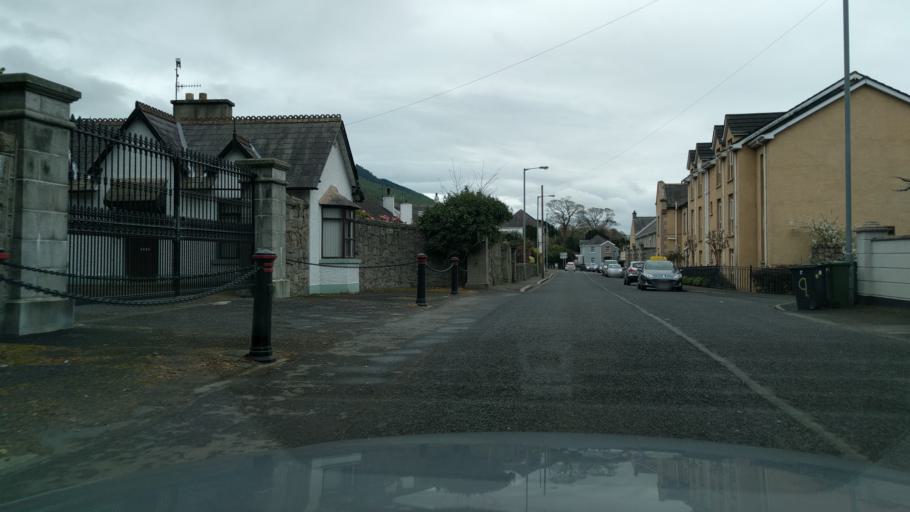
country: GB
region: Northern Ireland
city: Rostrevor
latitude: 54.1021
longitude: -6.2006
